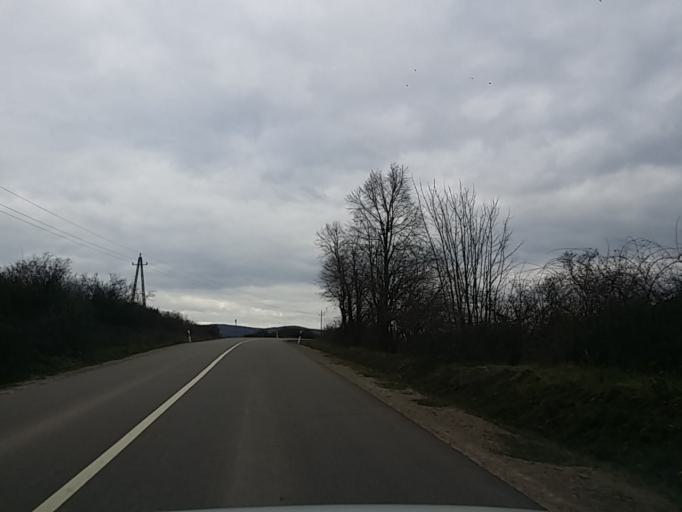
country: HU
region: Heves
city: Verpelet
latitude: 47.8568
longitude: 20.2070
